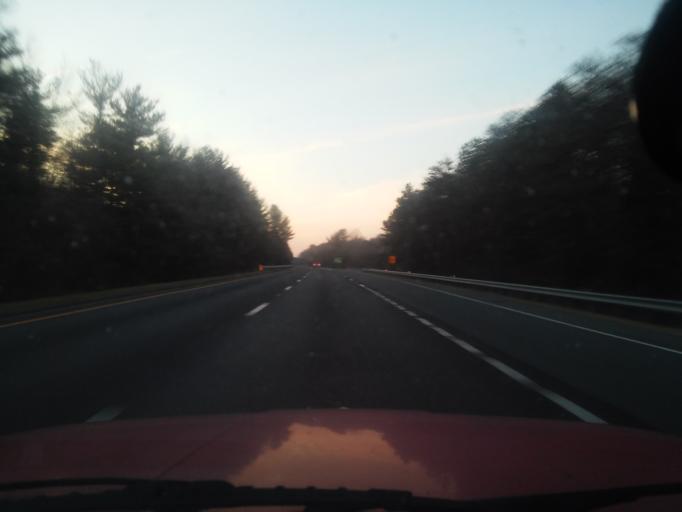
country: US
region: Virginia
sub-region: Louisa County
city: Louisa
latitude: 37.9378
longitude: -78.1027
